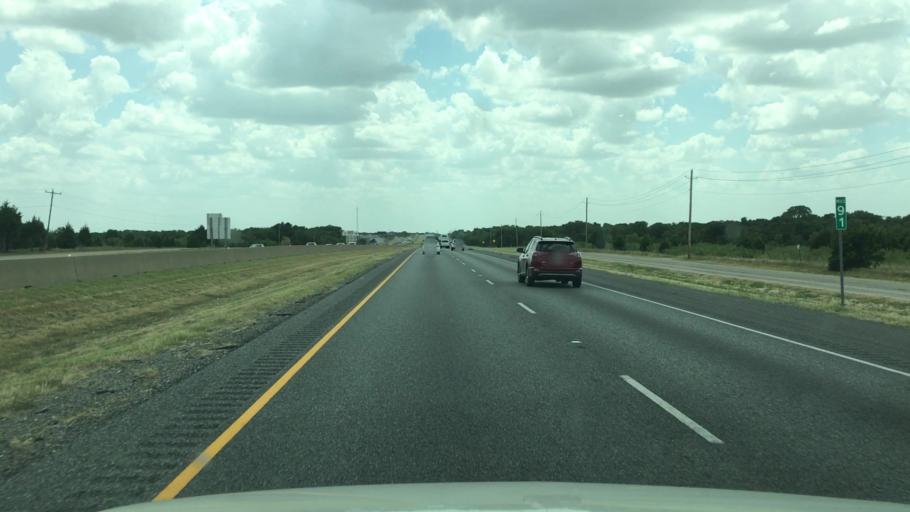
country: US
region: Texas
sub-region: Hunt County
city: Greenville
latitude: 33.0781
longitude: -96.1381
